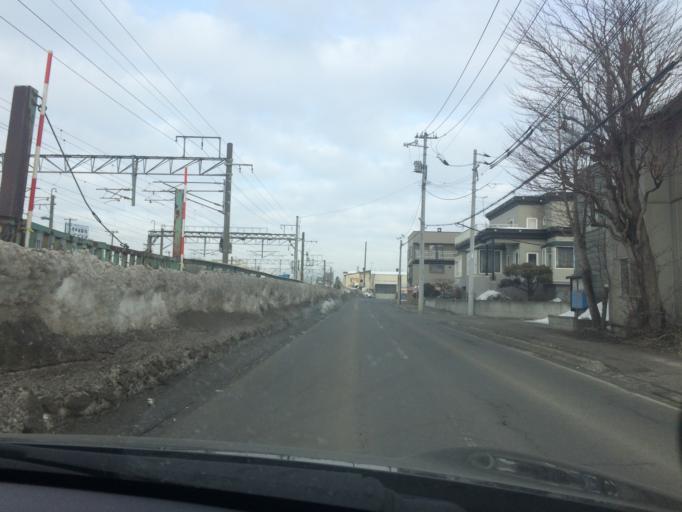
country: JP
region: Hokkaido
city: Sapporo
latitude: 43.0653
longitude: 141.3969
